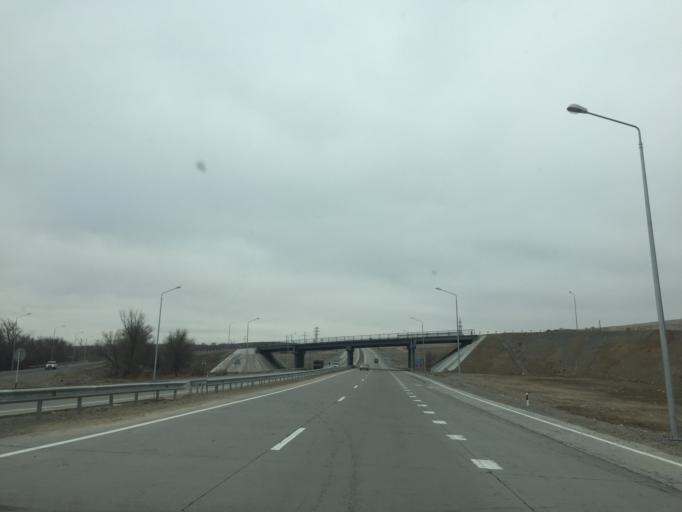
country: KZ
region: Ongtustik Qazaqstan
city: Sastobe
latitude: 42.5296
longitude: 70.0194
